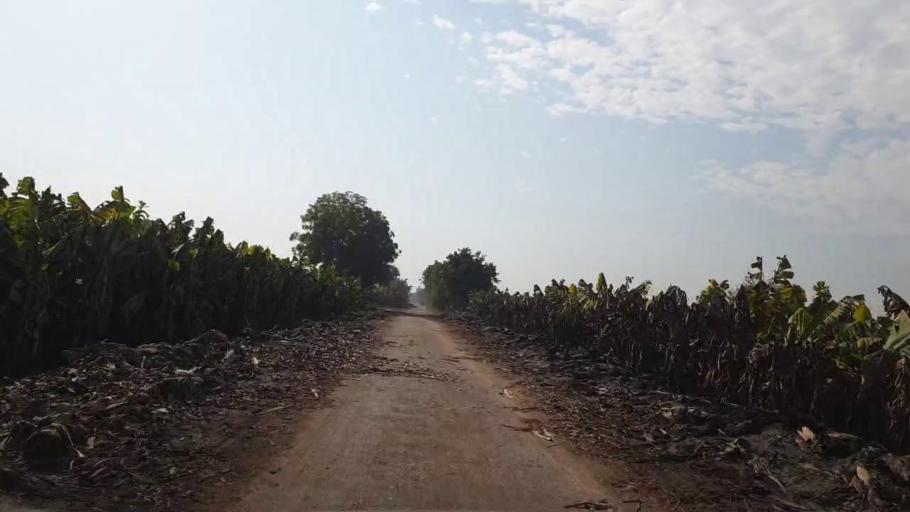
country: PK
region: Sindh
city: Matiari
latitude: 25.5567
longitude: 68.5159
